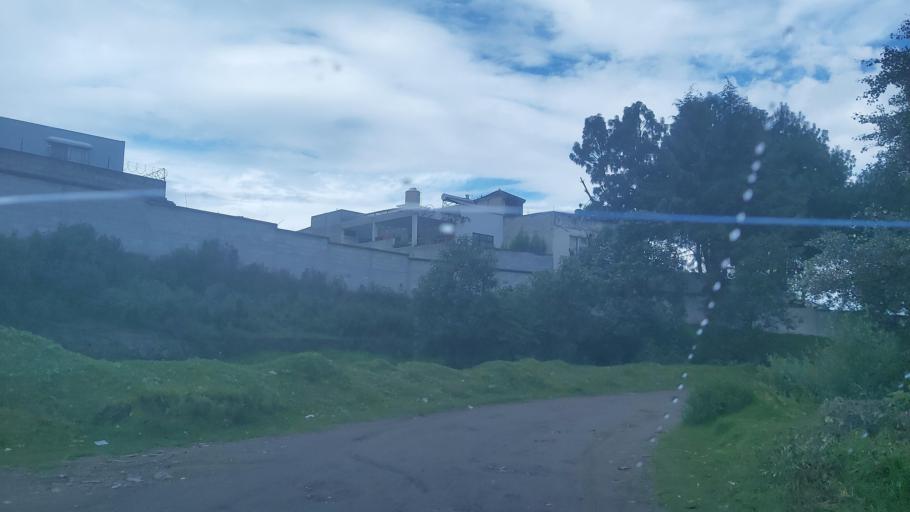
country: GT
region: Quetzaltenango
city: Quetzaltenango
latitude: 14.8531
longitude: -91.5405
